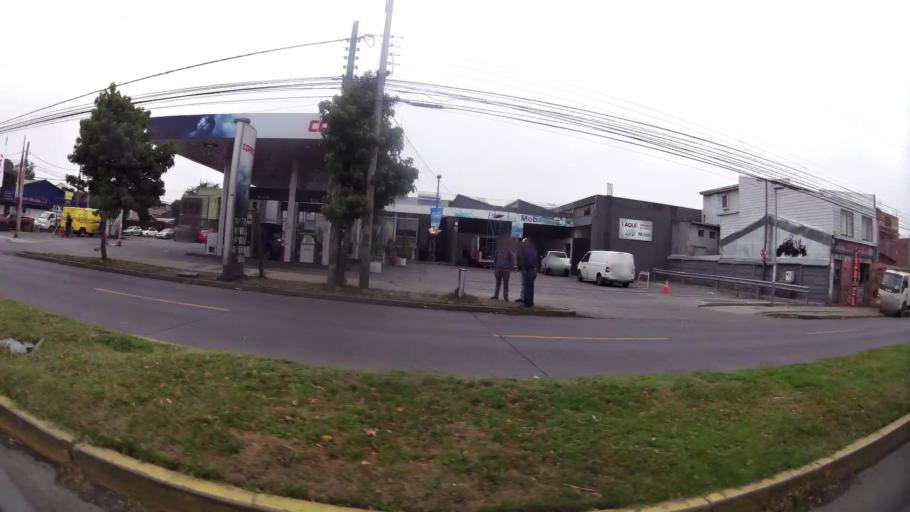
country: CL
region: Biobio
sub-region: Provincia de Concepcion
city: Concepcion
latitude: -36.8251
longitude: -73.0619
